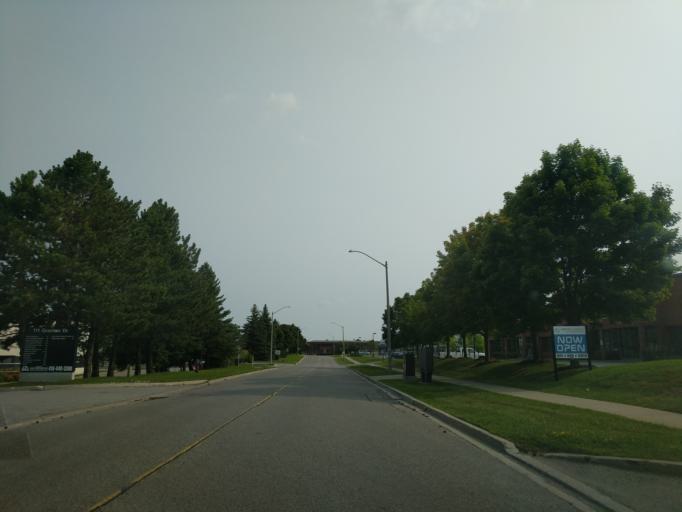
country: CA
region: Ontario
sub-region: York
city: Richmond Hill
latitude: 43.8590
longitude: -79.3886
